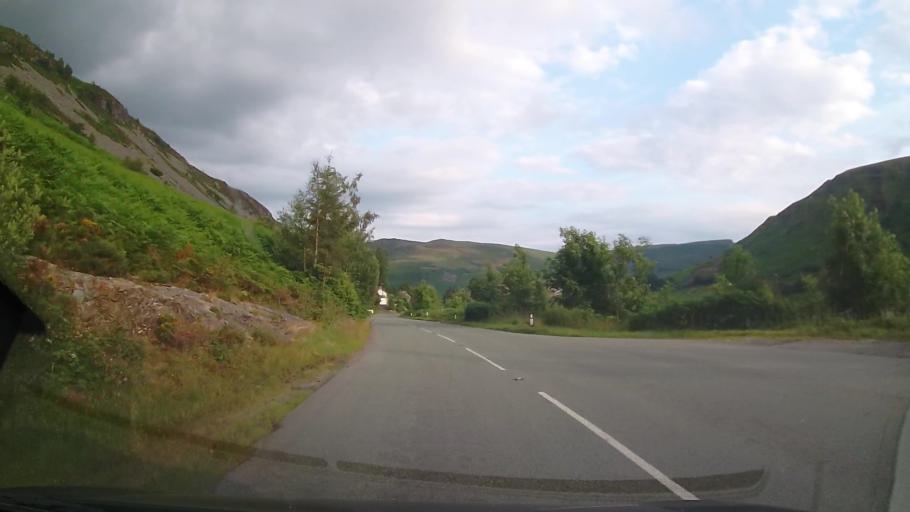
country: GB
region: Wales
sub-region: Sir Powys
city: Llangynog
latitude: 52.8334
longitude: -3.4179
